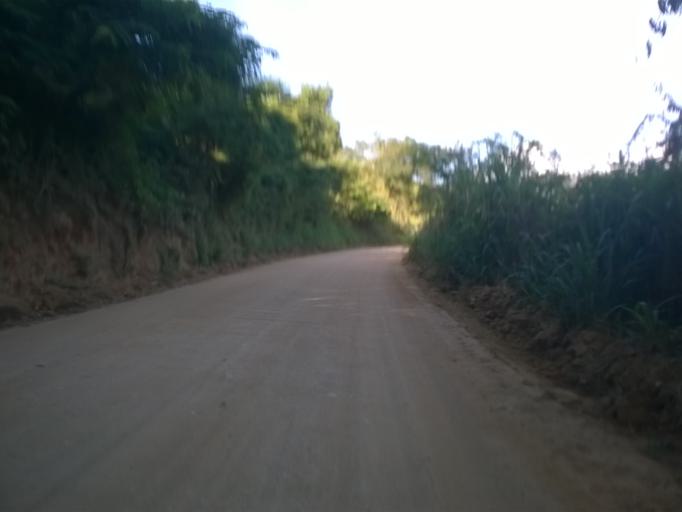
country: BR
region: Minas Gerais
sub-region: Uba
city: Uba
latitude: -21.0843
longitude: -43.0009
